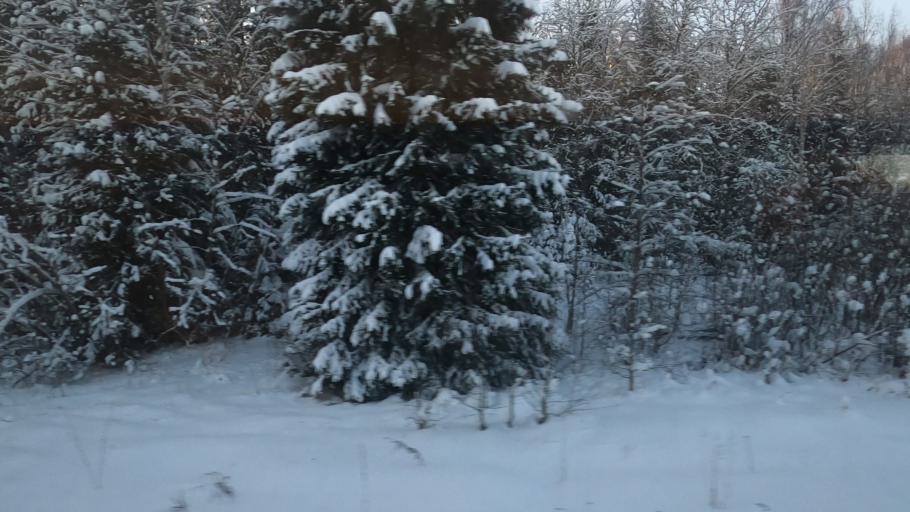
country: RU
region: Moskovskaya
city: Verbilki
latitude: 56.5282
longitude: 37.5590
